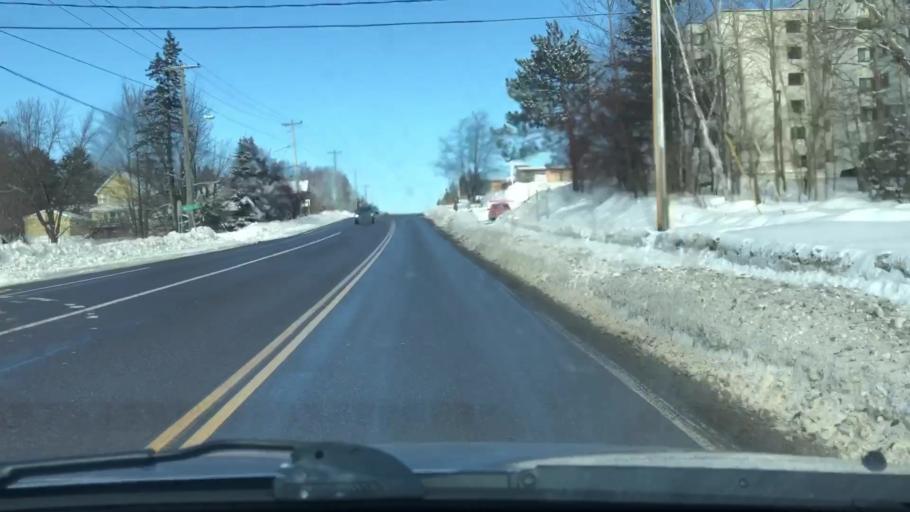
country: US
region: Minnesota
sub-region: Saint Louis County
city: Duluth
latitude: 46.8008
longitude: -92.1322
